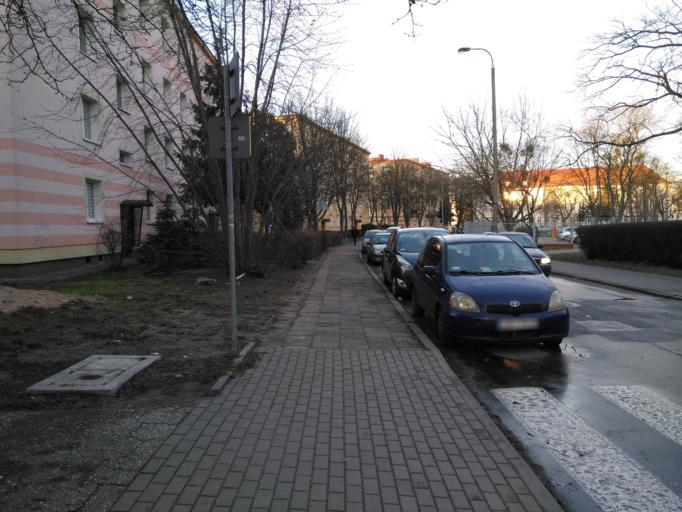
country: PL
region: Kujawsko-Pomorskie
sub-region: Bydgoszcz
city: Bydgoszcz
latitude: 53.1074
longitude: 18.0566
